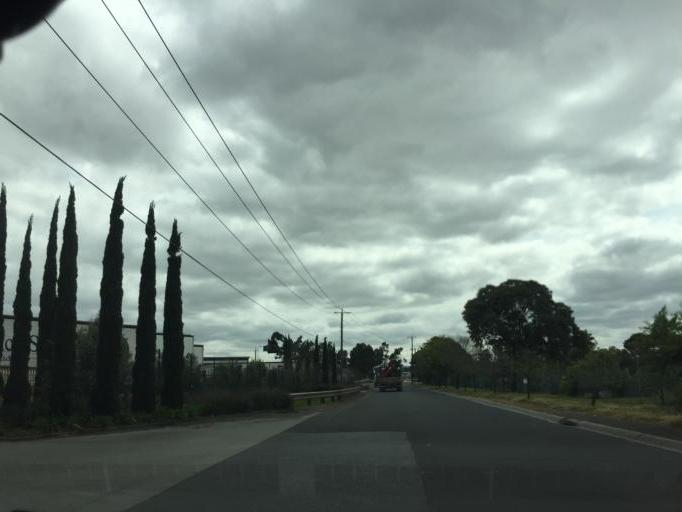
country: AU
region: Victoria
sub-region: Brimbank
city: Brooklyn
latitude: -37.8157
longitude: 144.8595
